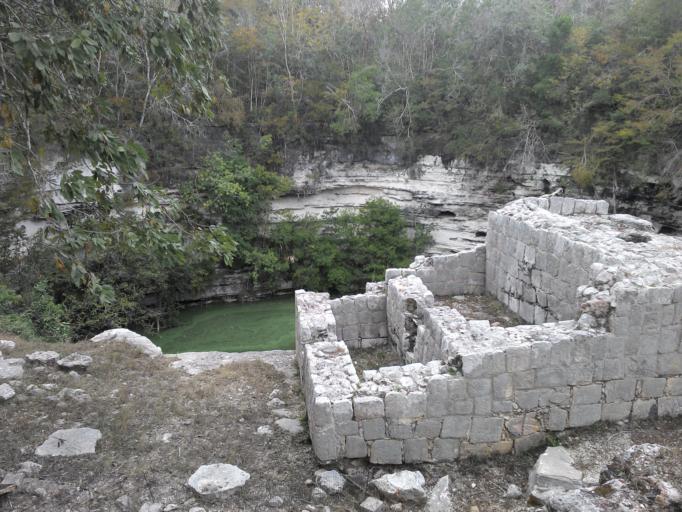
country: MX
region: Yucatan
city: Chichen-Itza
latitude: 20.6874
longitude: -88.5678
